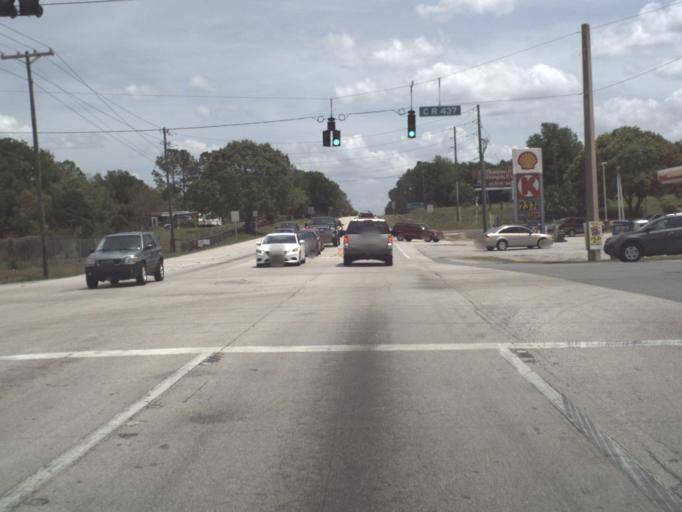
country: US
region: Florida
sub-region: Lake County
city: Mount Plymouth
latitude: 28.8515
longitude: -81.5518
